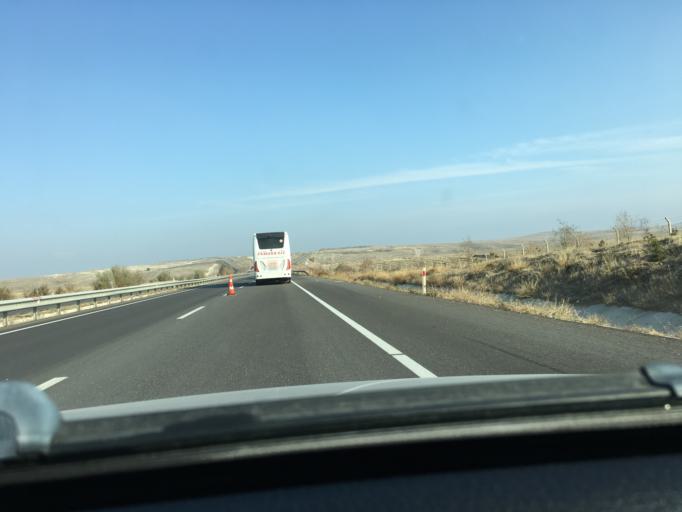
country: TR
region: Eskisehir
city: Gunyuzu
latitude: 39.5746
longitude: 31.8714
